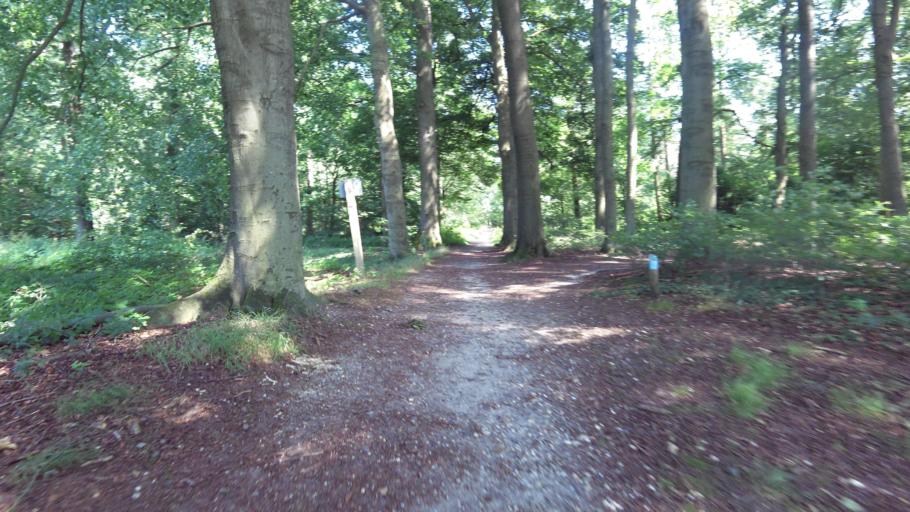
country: NL
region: Gelderland
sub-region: Gemeente Renkum
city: Oosterbeek
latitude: 51.9966
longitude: 5.8563
